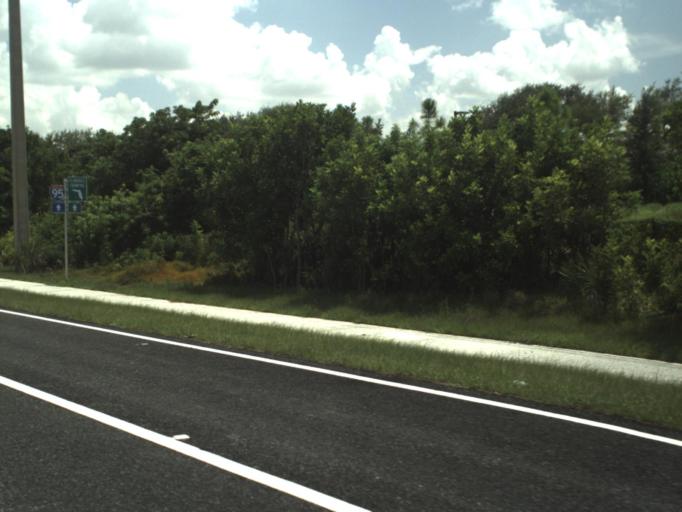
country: US
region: Florida
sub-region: Palm Beach County
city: Tequesta
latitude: 26.9891
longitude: -80.0941
